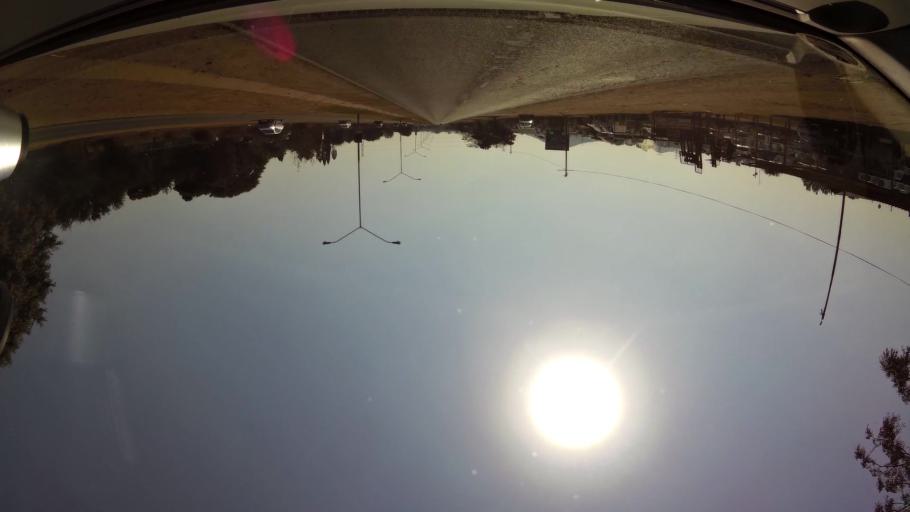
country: ZA
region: Gauteng
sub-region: City of Tshwane Metropolitan Municipality
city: Pretoria
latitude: -25.6671
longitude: 28.1928
